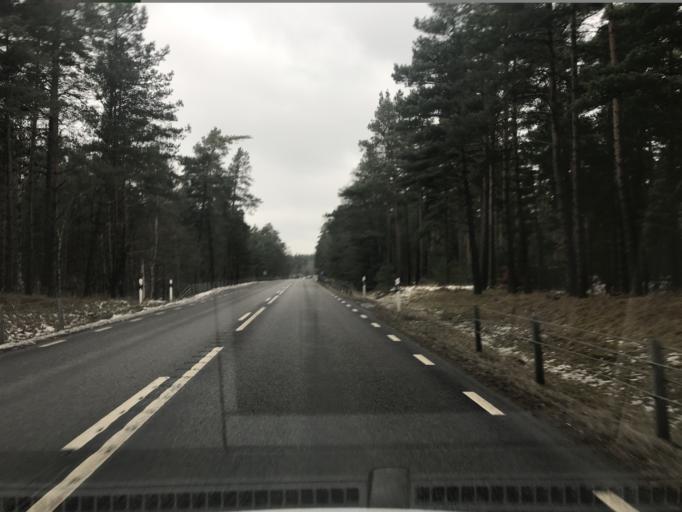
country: SE
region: Skane
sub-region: Kristianstads Kommun
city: Degeberga
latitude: 55.8550
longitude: 14.0932
